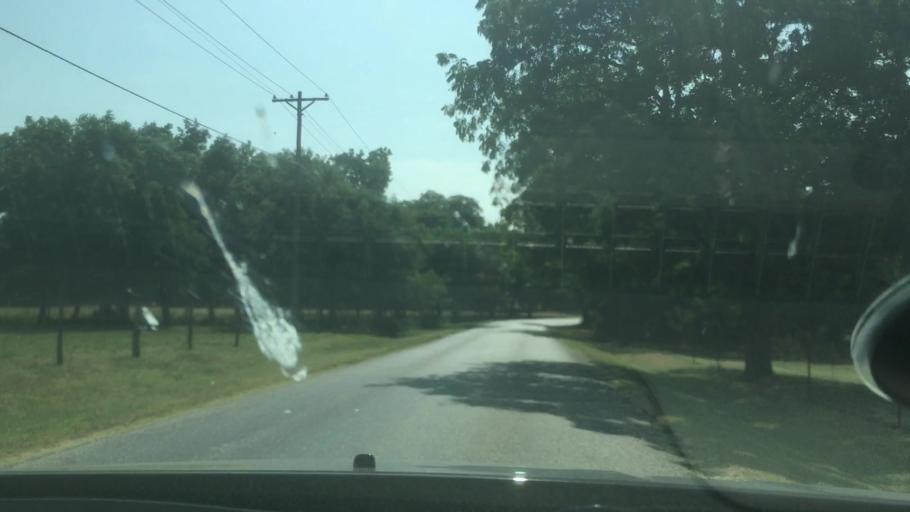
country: US
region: Texas
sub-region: Grayson County
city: Pottsboro
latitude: 33.8055
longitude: -96.6975
